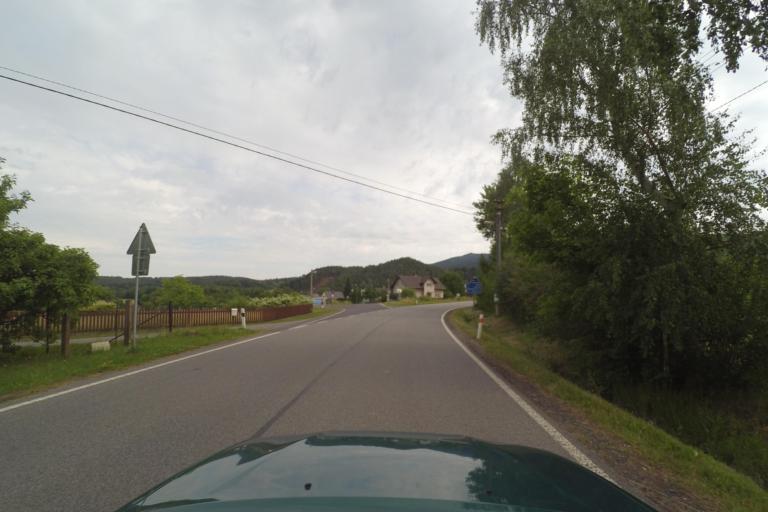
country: CZ
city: Osecna
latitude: 50.7078
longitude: 14.9662
